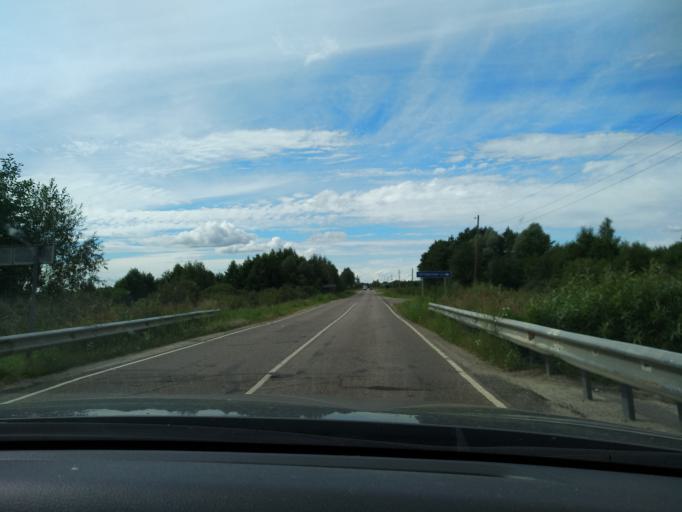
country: RU
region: Moskovskaya
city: Krasnyy Tkach
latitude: 55.3894
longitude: 39.1724
